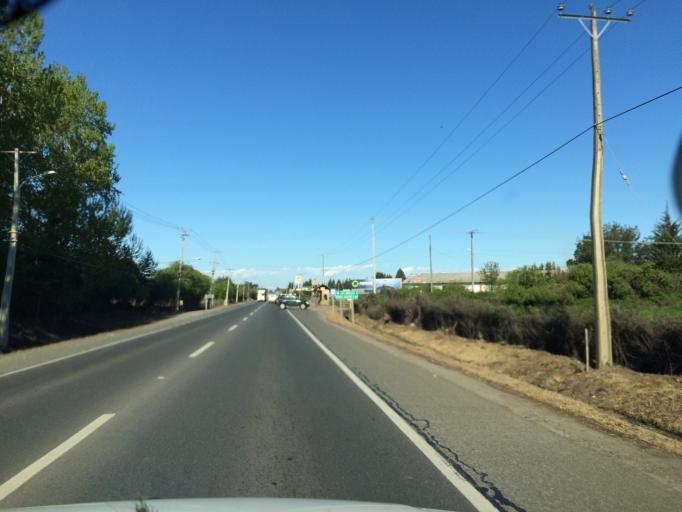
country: CL
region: Biobio
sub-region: Provincia de Biobio
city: Los Angeles
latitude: -37.4818
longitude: -72.4405
